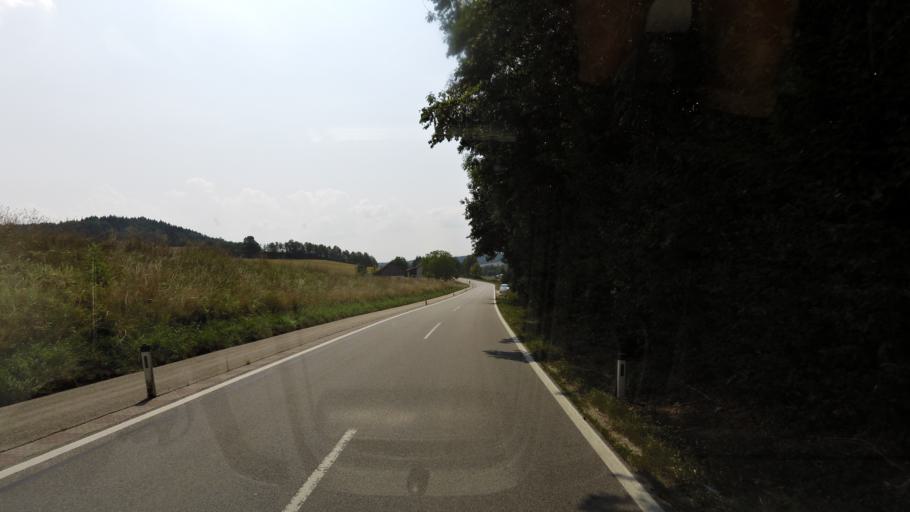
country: DE
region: Bavaria
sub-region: Lower Bavaria
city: Bad Fussing
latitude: 48.2585
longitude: 13.3358
